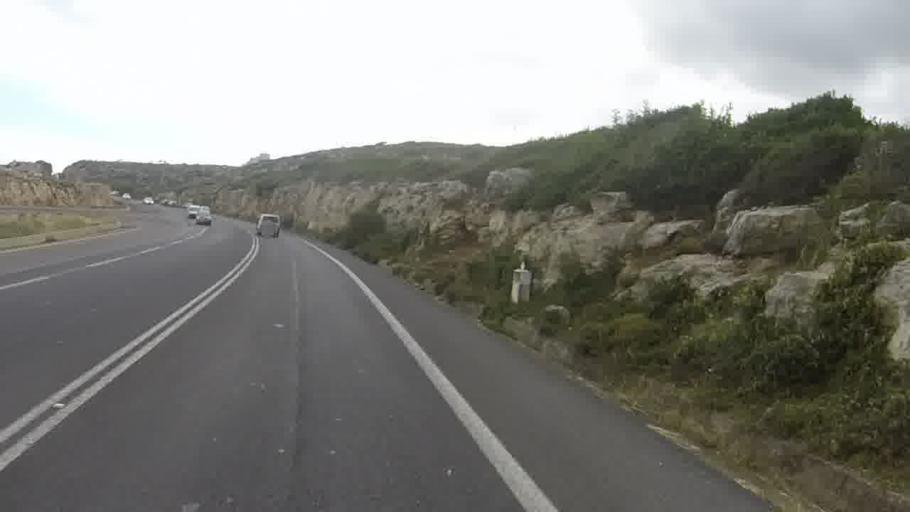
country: GR
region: Crete
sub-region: Nomos Rethymnis
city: Atsipopoulon
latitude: 35.3584
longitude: 24.4086
